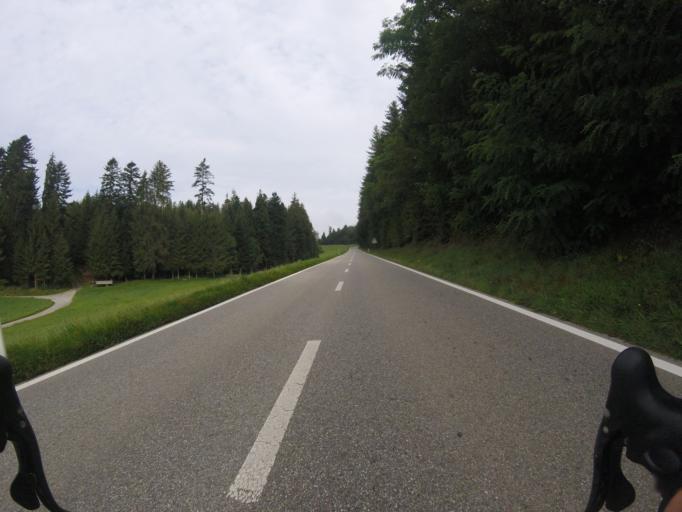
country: CH
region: Bern
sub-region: Bern-Mittelland District
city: Biglen
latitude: 46.9430
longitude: 7.6522
